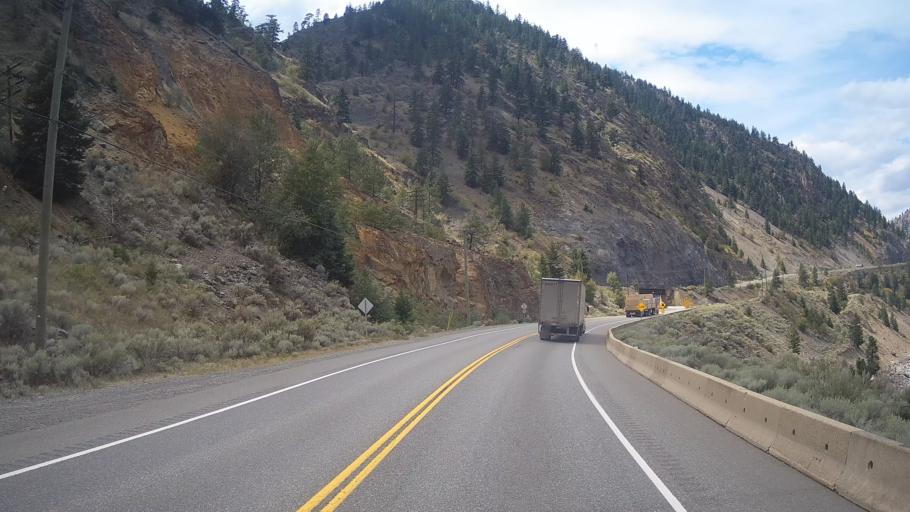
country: CA
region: British Columbia
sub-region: Thompson-Nicola Regional District
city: Ashcroft
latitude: 50.2547
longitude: -121.4411
